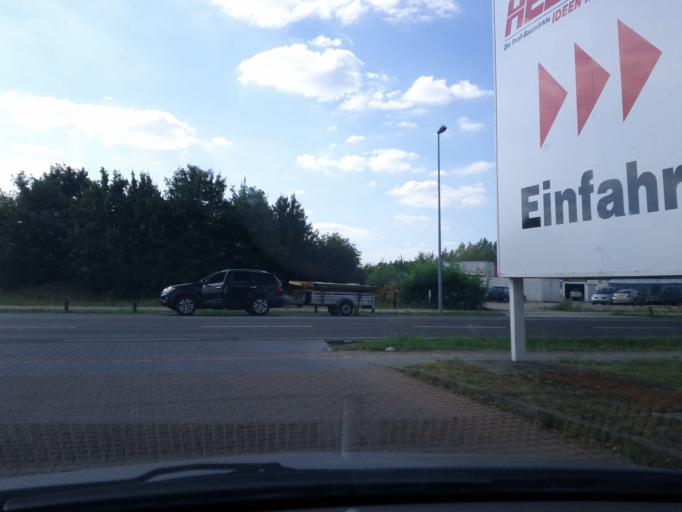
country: DE
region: Berlin
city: Mahlsdorf
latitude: 52.5043
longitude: 13.6329
